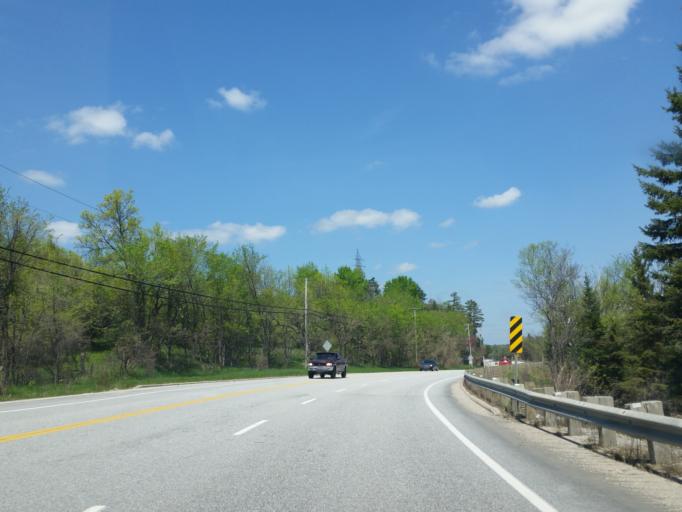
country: CA
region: Quebec
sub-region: Outaouais
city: Wakefield
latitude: 45.6648
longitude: -75.9279
